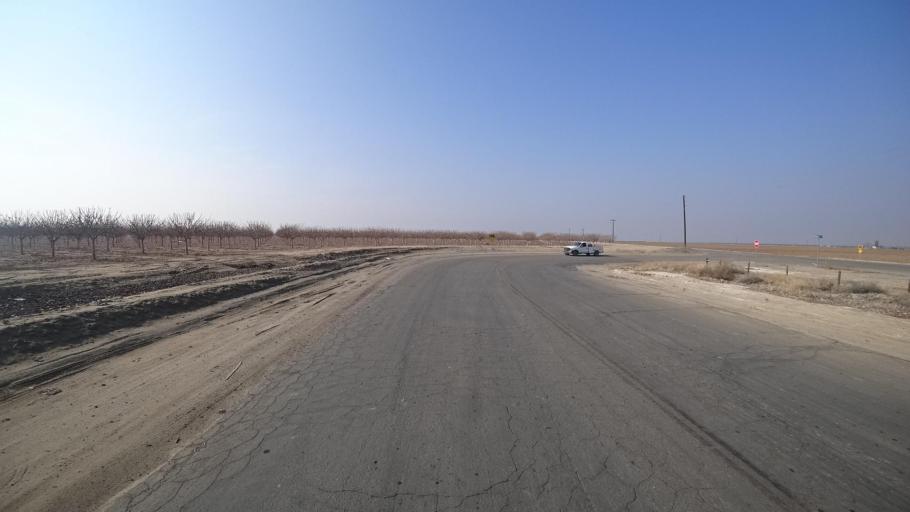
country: US
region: California
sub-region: Kern County
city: Buttonwillow
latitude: 35.4420
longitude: -119.4607
